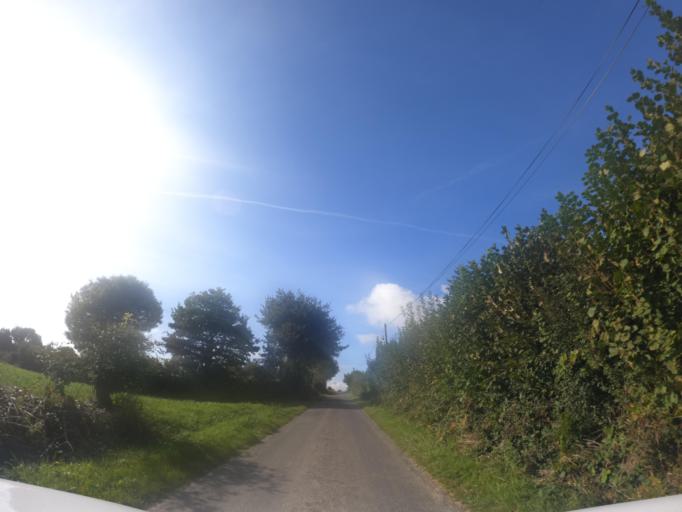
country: FR
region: Poitou-Charentes
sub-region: Departement des Deux-Sevres
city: Courlay
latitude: 46.7893
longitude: -0.5788
